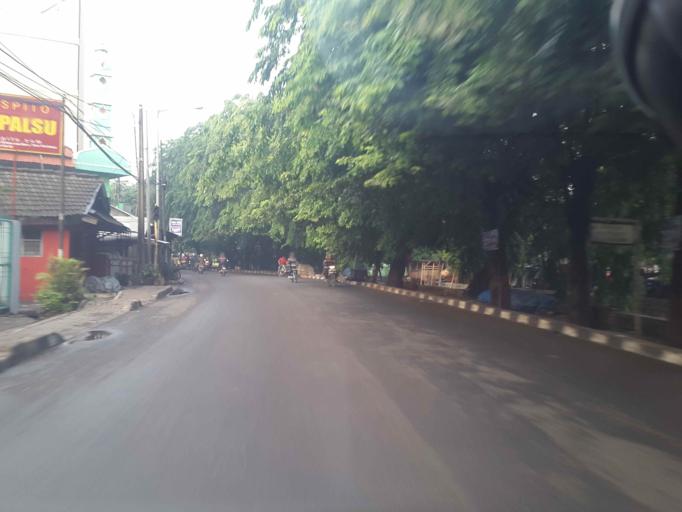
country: ID
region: West Java
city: Bekasi
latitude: -6.2464
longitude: 107.0114
